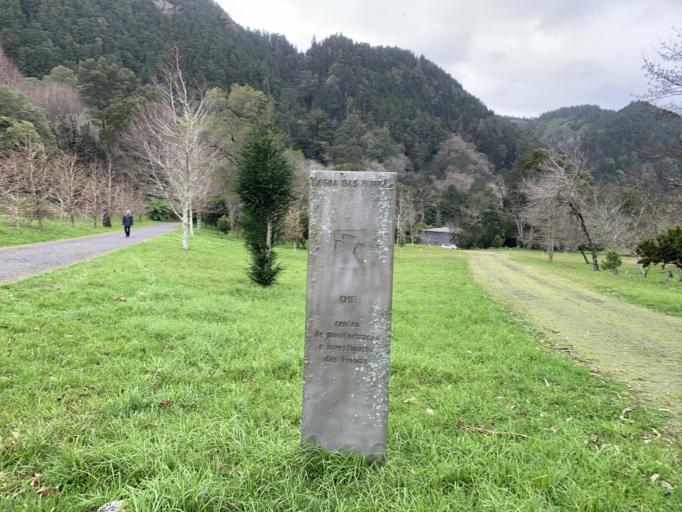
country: PT
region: Azores
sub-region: Povoacao
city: Furnas
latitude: 37.7509
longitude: -25.3360
